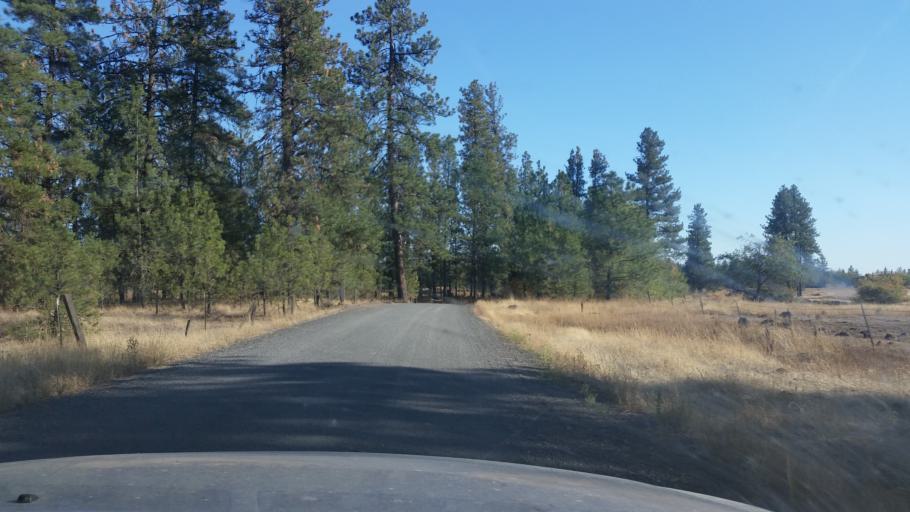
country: US
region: Washington
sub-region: Spokane County
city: Cheney
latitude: 47.4294
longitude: -117.6538
